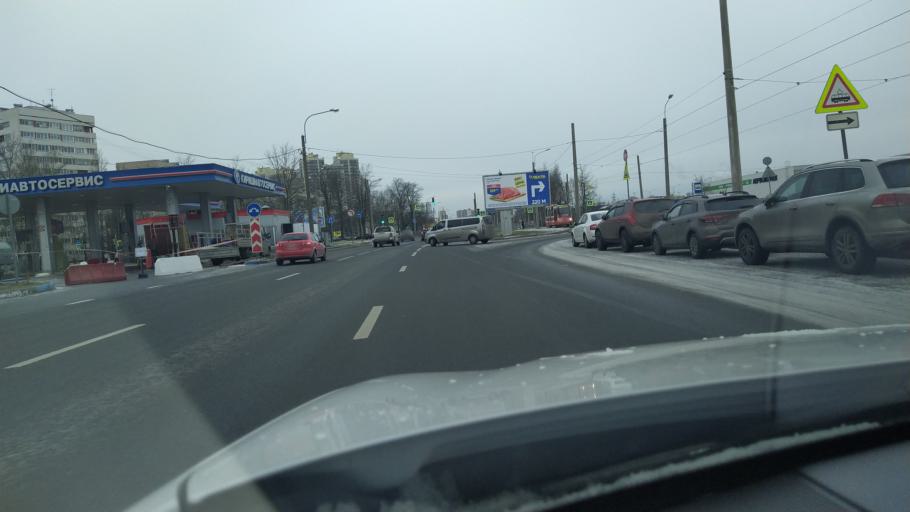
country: RU
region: St.-Petersburg
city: Grazhdanka
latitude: 60.0259
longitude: 30.4321
